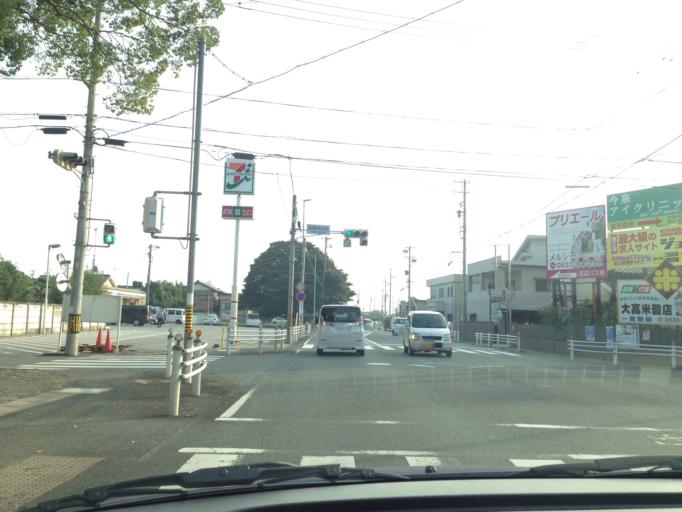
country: JP
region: Aichi
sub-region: Tokai-shi
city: Toyokawa
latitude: 34.8478
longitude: 137.4184
